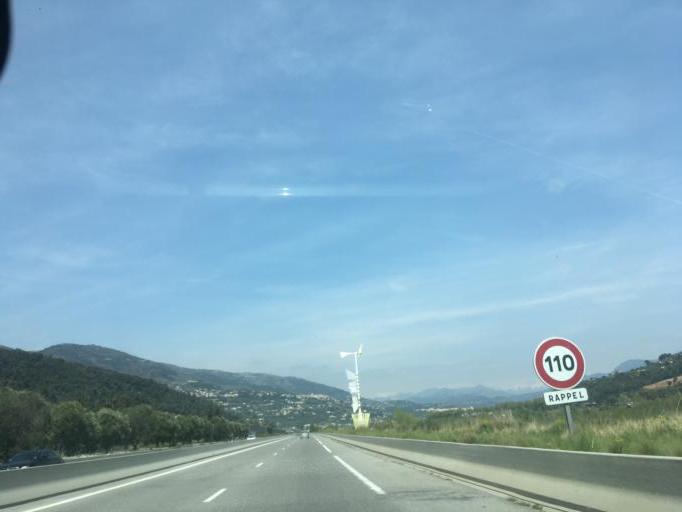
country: FR
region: Provence-Alpes-Cote d'Azur
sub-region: Departement des Alpes-Maritimes
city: La Gaude
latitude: 43.7241
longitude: 7.1817
